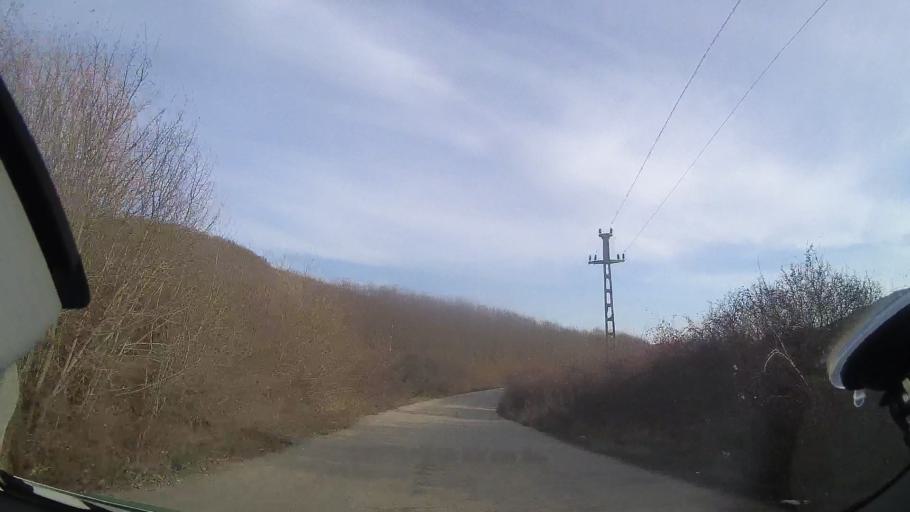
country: RO
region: Bihor
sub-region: Comuna Sarbi
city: Sarbi
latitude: 47.1815
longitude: 22.1341
